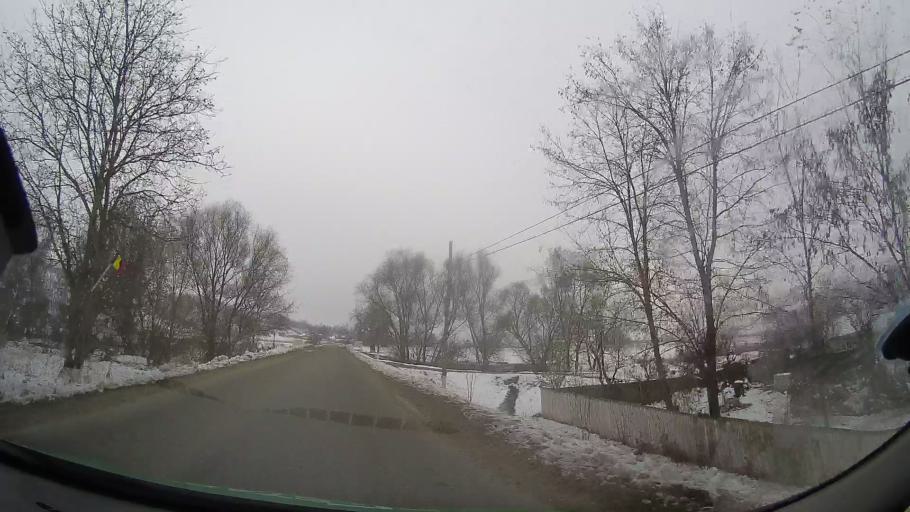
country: RO
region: Bacau
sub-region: Comuna Glavanesti
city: Frumuselu
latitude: 46.2943
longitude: 27.3006
